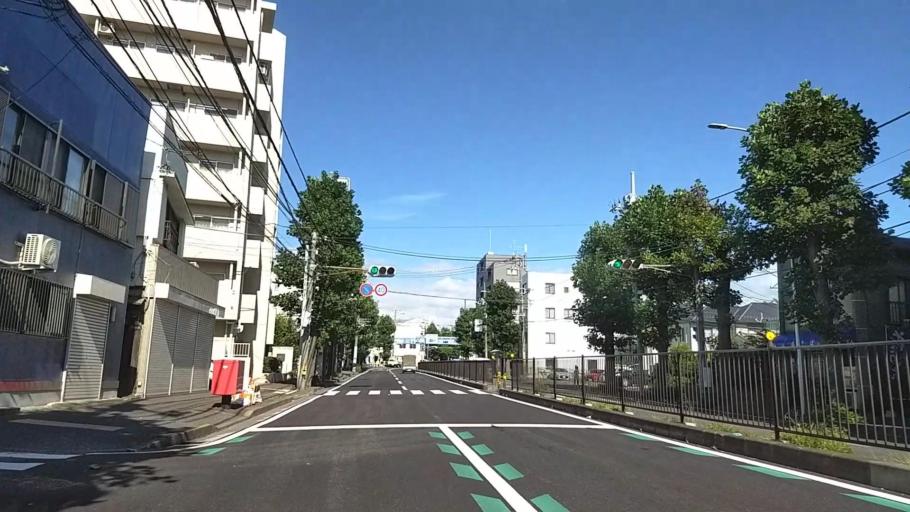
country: JP
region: Kanagawa
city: Yokohama
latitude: 35.4897
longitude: 139.6227
